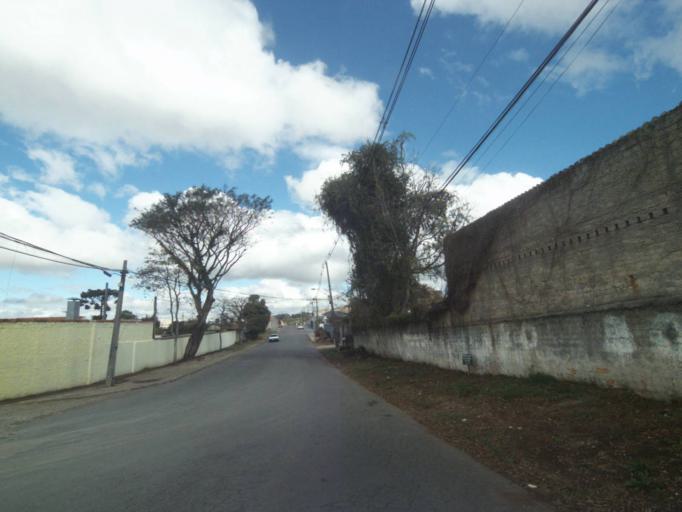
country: BR
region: Parana
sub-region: Sao Jose Dos Pinhais
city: Sao Jose dos Pinhais
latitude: -25.5352
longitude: -49.2942
